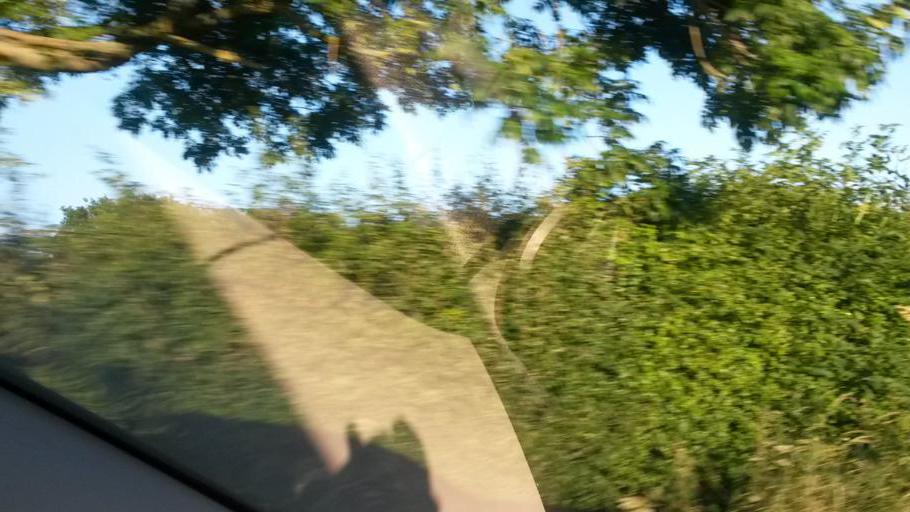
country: IE
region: Leinster
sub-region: An Mhi
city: Ashbourne
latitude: 53.4800
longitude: -6.3162
